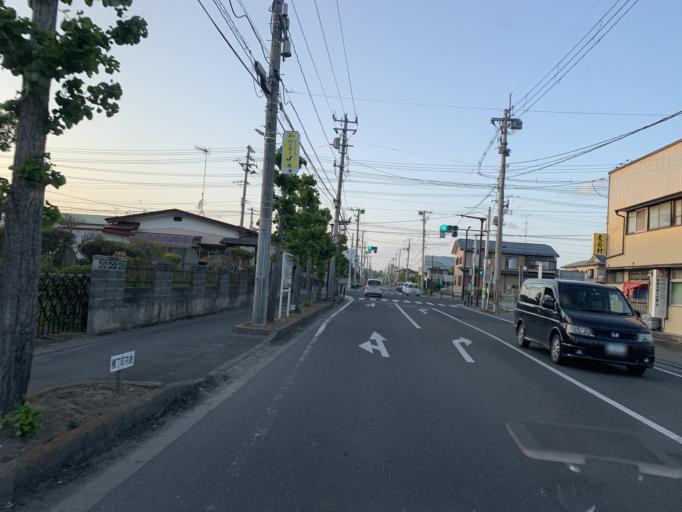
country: JP
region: Miyagi
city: Wakuya
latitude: 38.6847
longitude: 141.1945
